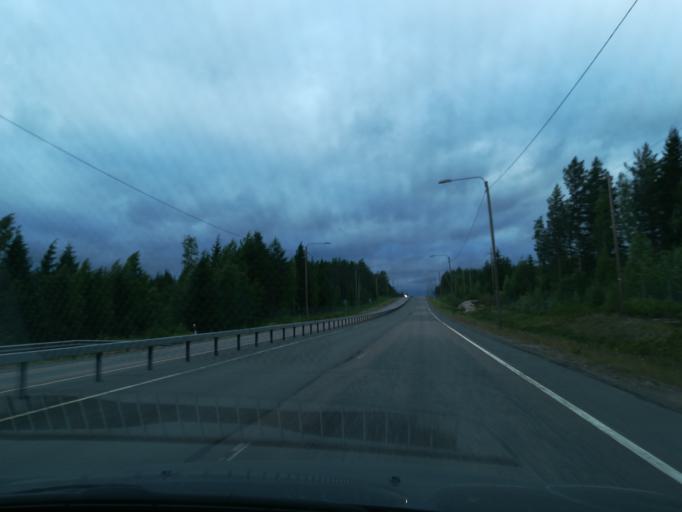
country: FI
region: Southern Savonia
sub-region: Mikkeli
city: Ristiina
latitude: 61.4064
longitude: 27.3520
